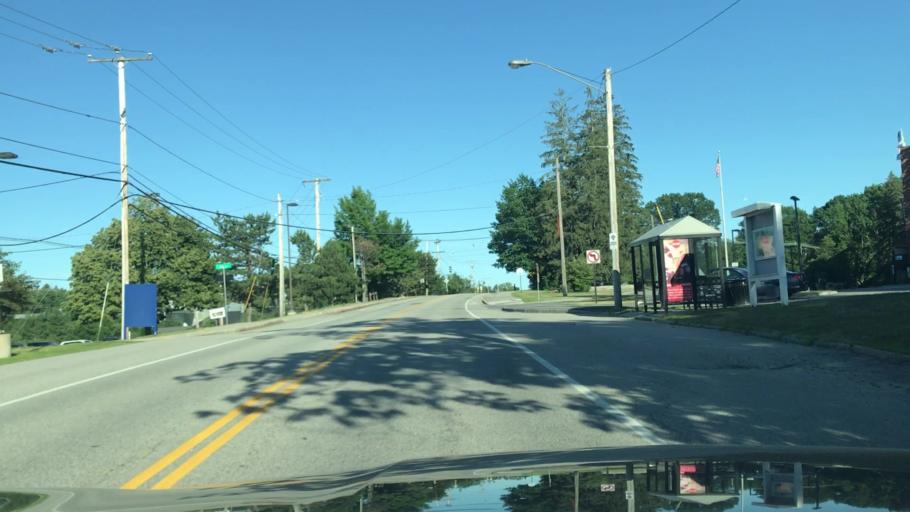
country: US
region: New Hampshire
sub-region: Strafford County
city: Durham
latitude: 43.1397
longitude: -70.9384
